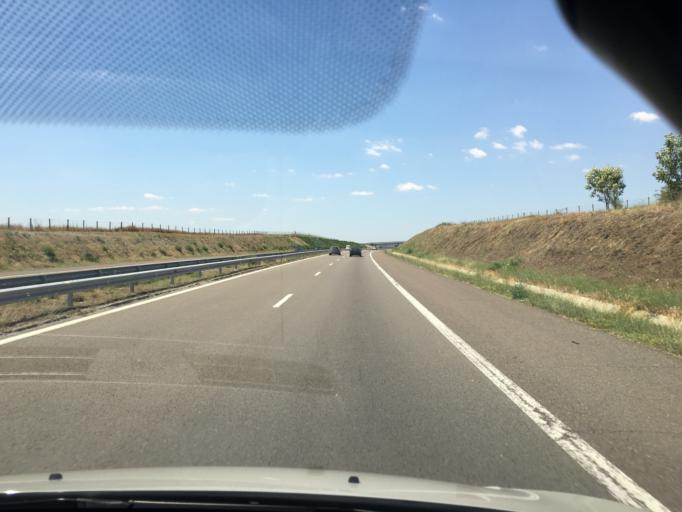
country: BG
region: Burgas
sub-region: Obshtina Kameno
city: Kameno
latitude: 42.5869
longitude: 27.1923
